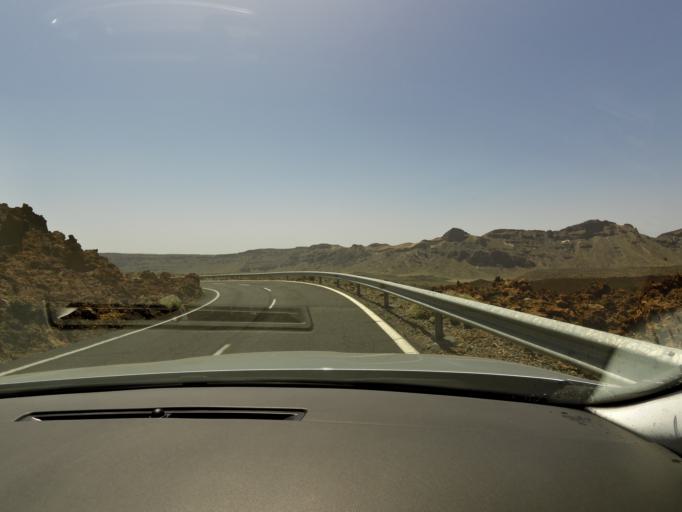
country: ES
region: Canary Islands
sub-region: Provincia de Santa Cruz de Tenerife
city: Vilaflor
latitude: 28.2591
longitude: -16.5997
